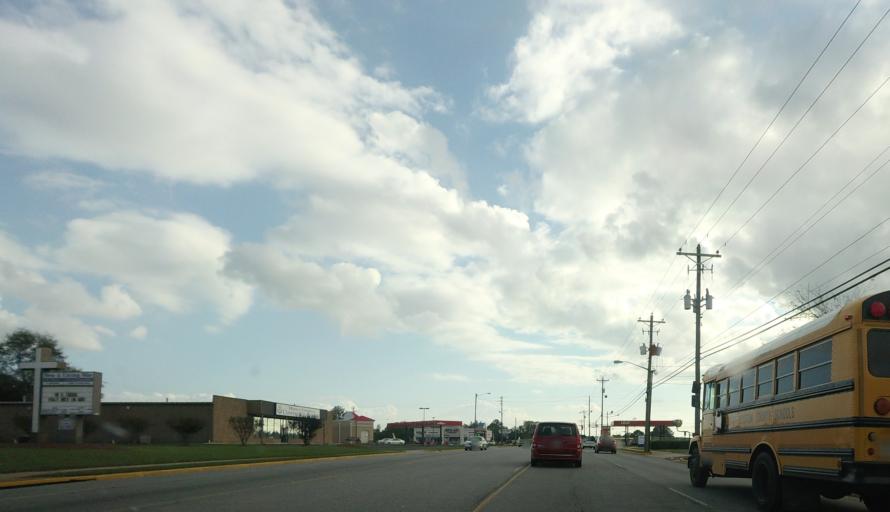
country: US
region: Georgia
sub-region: Houston County
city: Warner Robins
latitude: 32.6278
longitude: -83.6416
